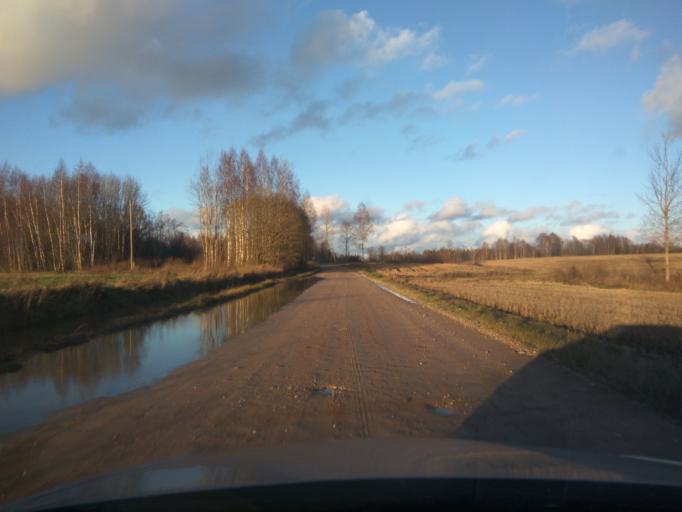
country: LV
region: Aizpute
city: Aizpute
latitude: 56.7739
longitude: 21.7860
